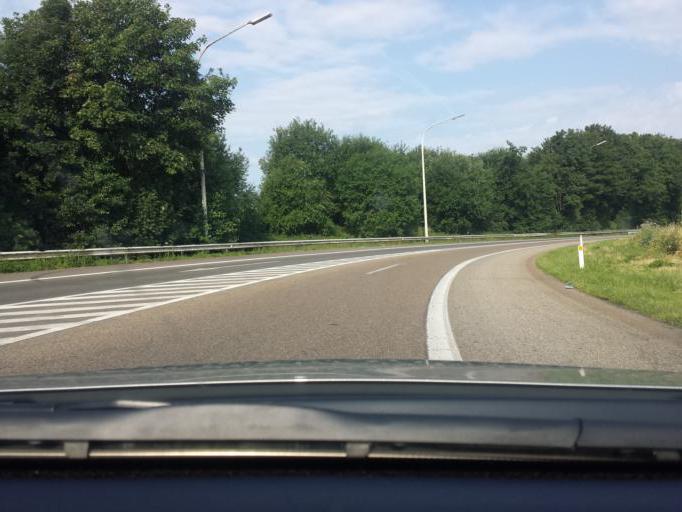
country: BE
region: Flanders
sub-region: Provincie Limburg
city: Tongeren
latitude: 50.7903
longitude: 5.5310
